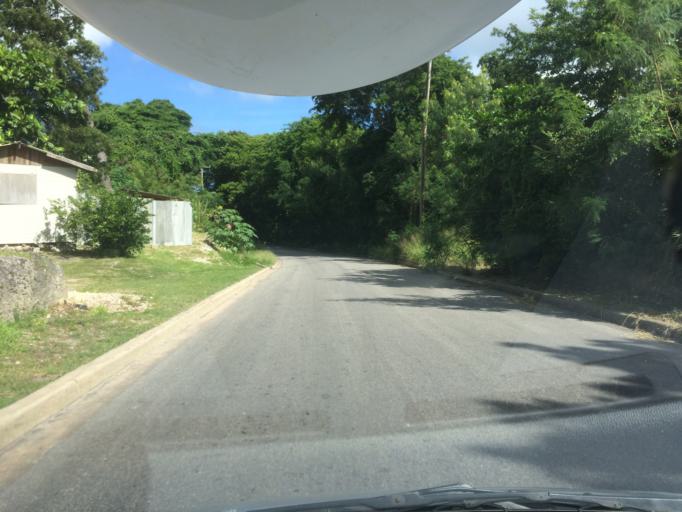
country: BB
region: Saint Lucy
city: Checker Hall
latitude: 13.2953
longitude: -59.6417
